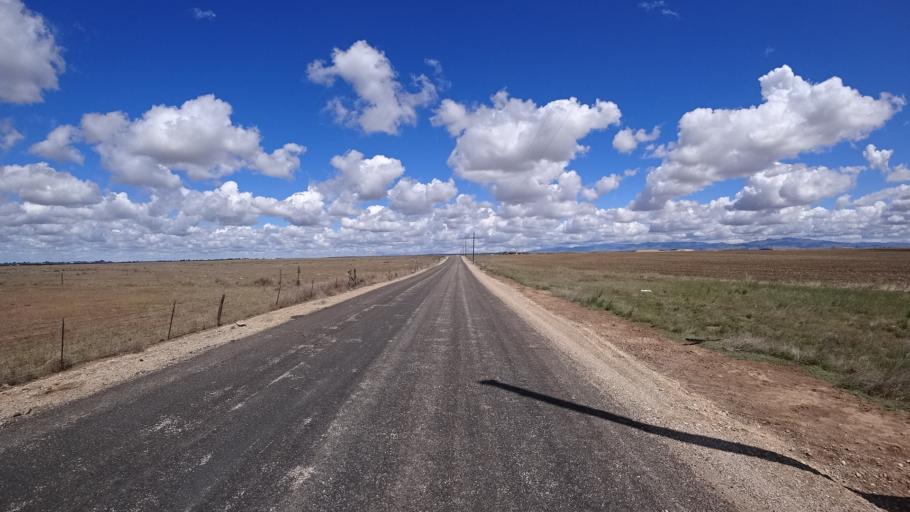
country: US
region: Idaho
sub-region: Ada County
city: Kuna
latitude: 43.4615
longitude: -116.2744
